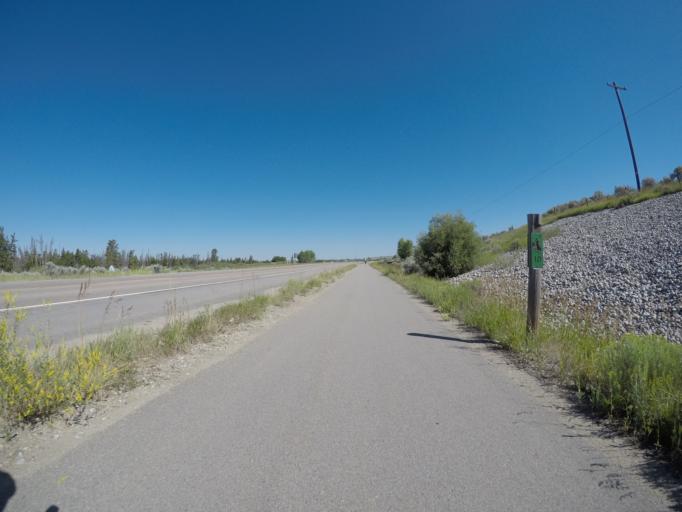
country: US
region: Wyoming
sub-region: Sublette County
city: Pinedale
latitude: 42.8500
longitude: -109.8496
